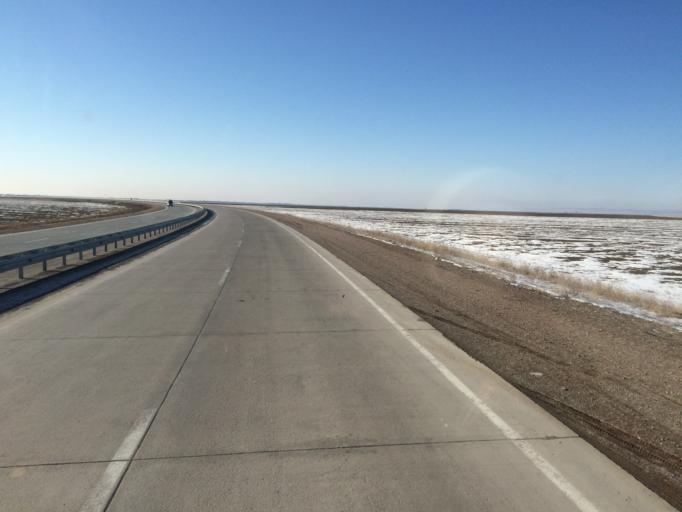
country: KG
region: Chuy
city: Sokuluk
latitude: 43.3463
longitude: 74.2986
